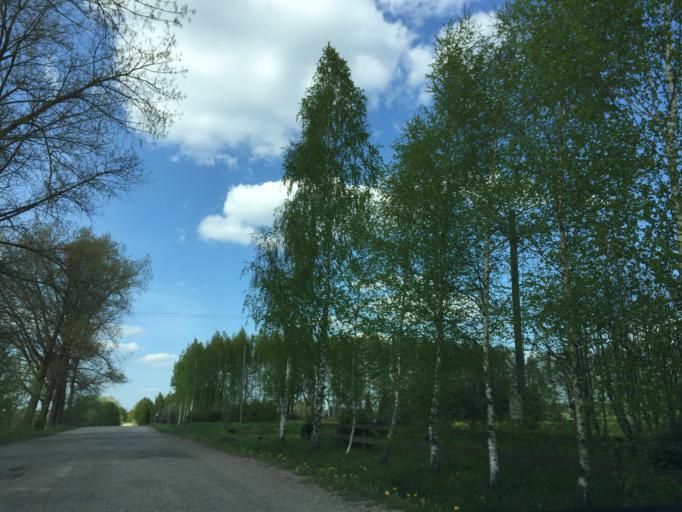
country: LV
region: Vecumnieki
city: Vecumnieki
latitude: 56.4337
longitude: 24.4096
